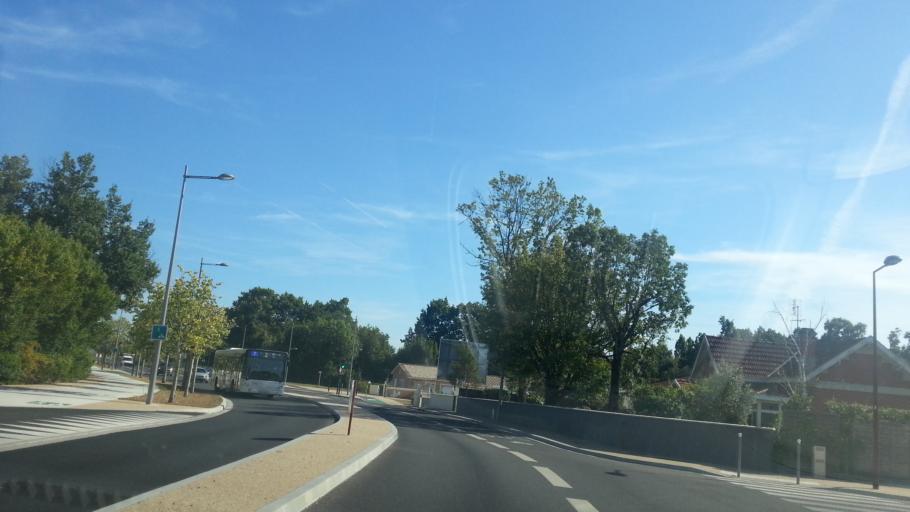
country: FR
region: Aquitaine
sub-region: Departement de la Gironde
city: Bassens
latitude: 44.8950
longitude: -0.5169
